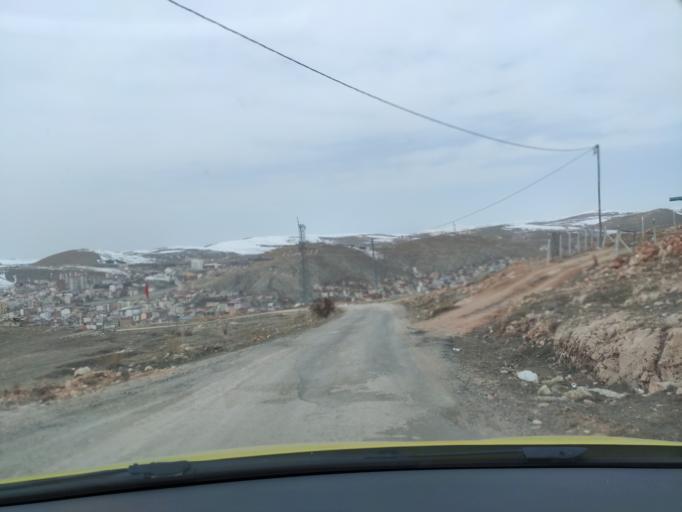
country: TR
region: Bayburt
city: Bayburt
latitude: 40.2586
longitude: 40.2367
